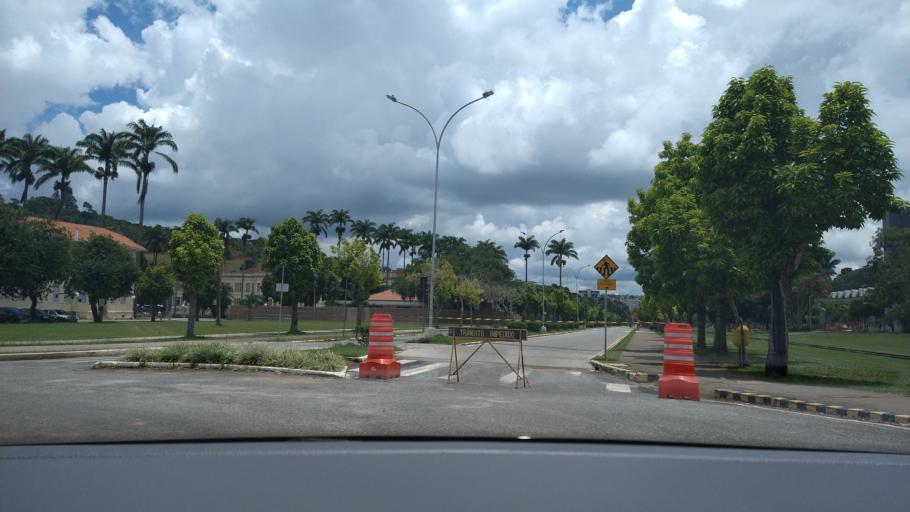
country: BR
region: Minas Gerais
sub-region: Vicosa
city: Vicosa
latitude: -20.7625
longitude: -42.8671
